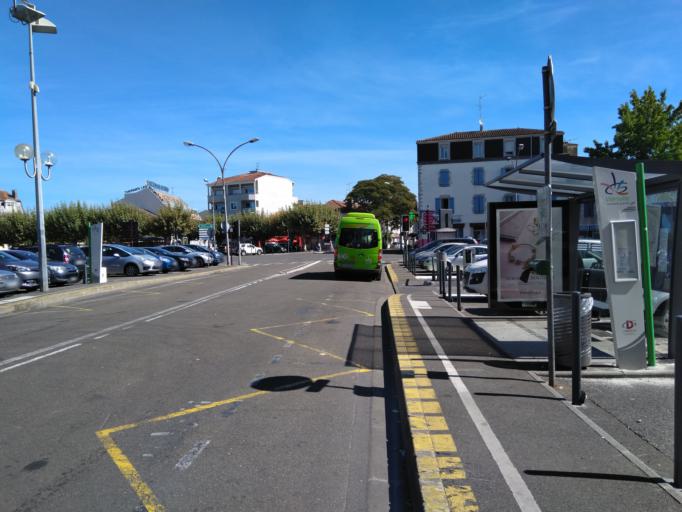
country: FR
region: Aquitaine
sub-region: Departement des Landes
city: Dax
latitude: 43.7088
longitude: -1.0505
